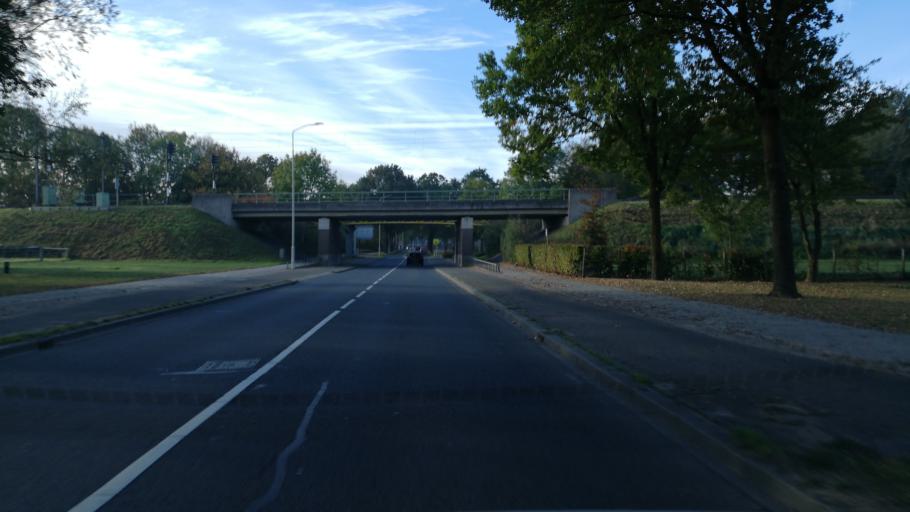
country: NL
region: Gelderland
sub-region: Gemeente Westervoort
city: Westervoort
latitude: 51.9572
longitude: 5.9822
